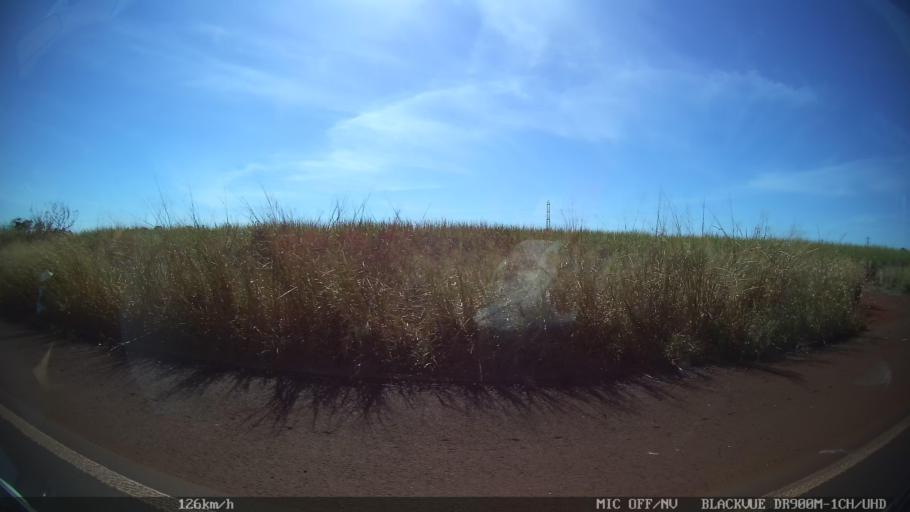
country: BR
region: Sao Paulo
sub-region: Guaira
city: Guaira
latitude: -20.4453
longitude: -48.3981
